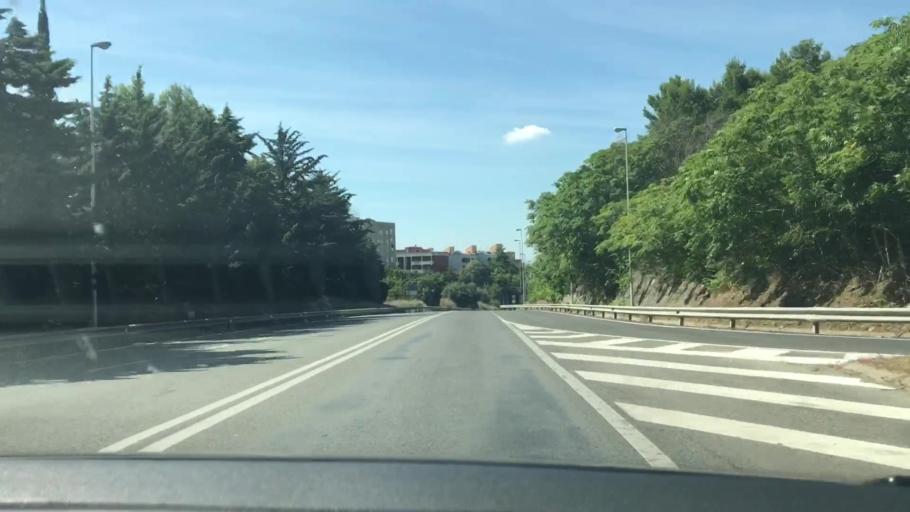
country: IT
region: Basilicate
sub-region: Provincia di Matera
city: Matera
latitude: 40.6791
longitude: 16.5852
